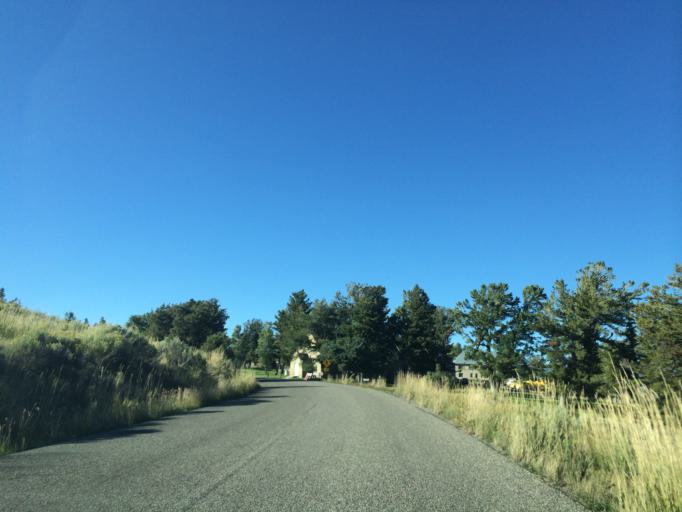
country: US
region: Montana
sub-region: Gallatin County
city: West Yellowstone
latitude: 44.9716
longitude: -110.6978
